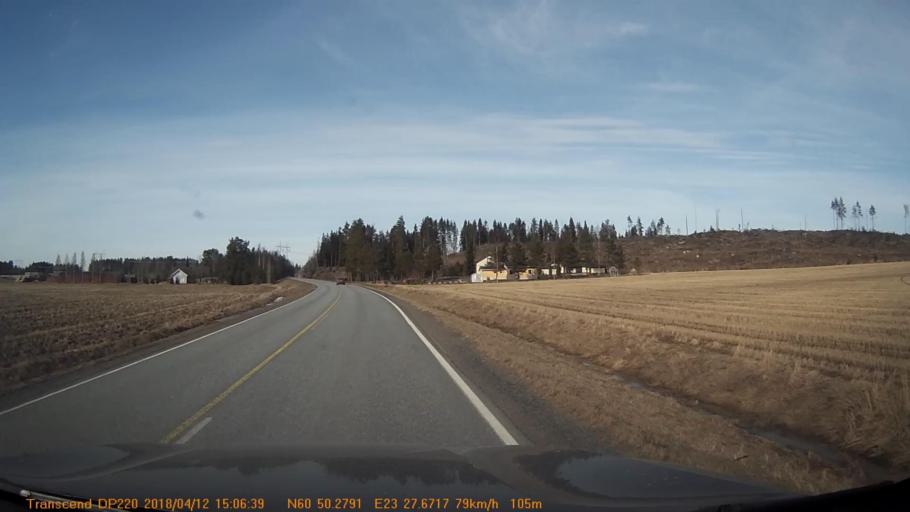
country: FI
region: Haeme
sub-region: Forssa
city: Jokioinen
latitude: 60.8385
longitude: 23.4613
